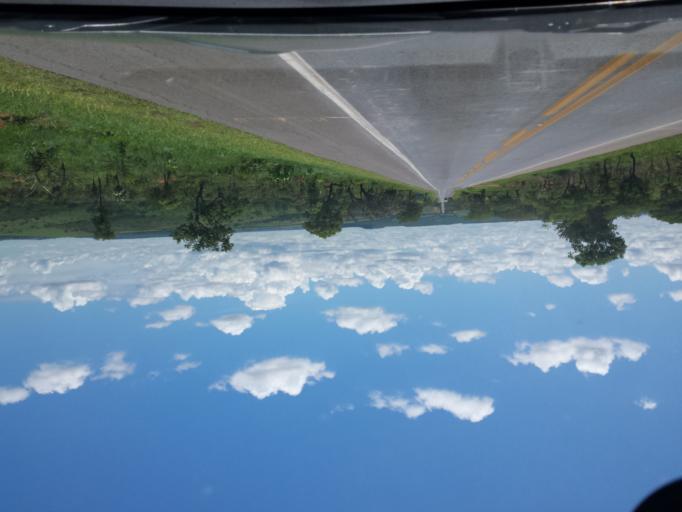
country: BR
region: Goias
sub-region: Cristalina
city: Cristalina
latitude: -16.5715
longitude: -47.7892
